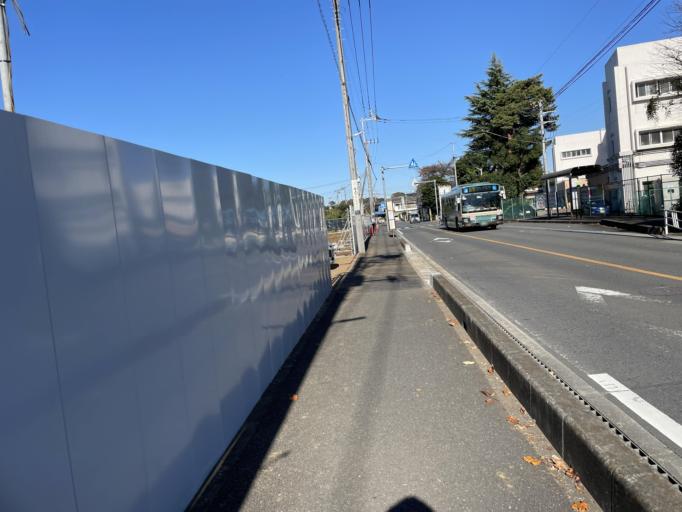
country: JP
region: Saitama
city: Asaka
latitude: 35.7840
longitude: 139.5596
